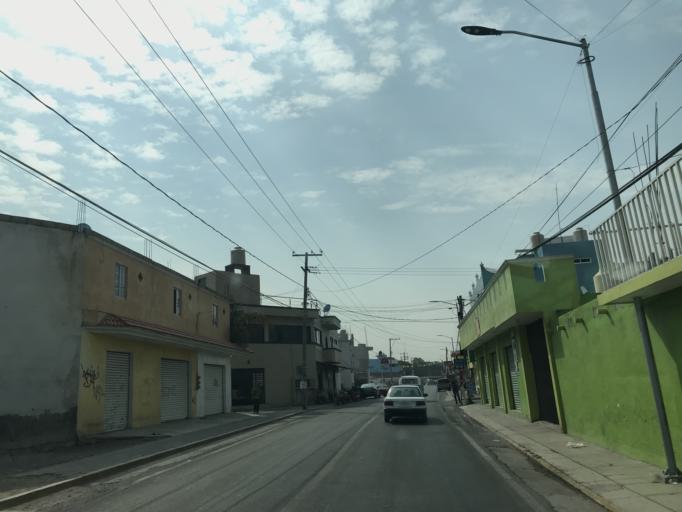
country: MX
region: Tlaxcala
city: Tenancingo
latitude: 19.1432
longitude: -98.1932
